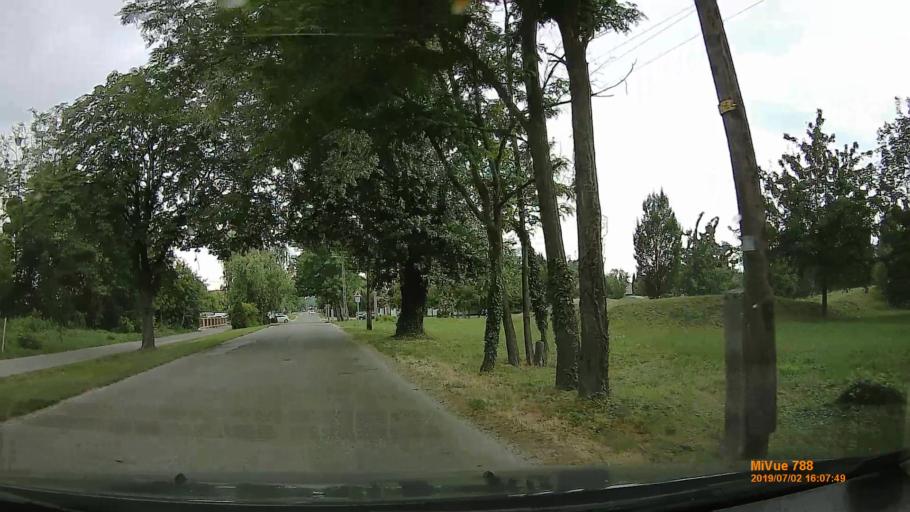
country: HU
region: Gyor-Moson-Sopron
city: Mosonmagyarovar
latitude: 47.8722
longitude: 17.2879
